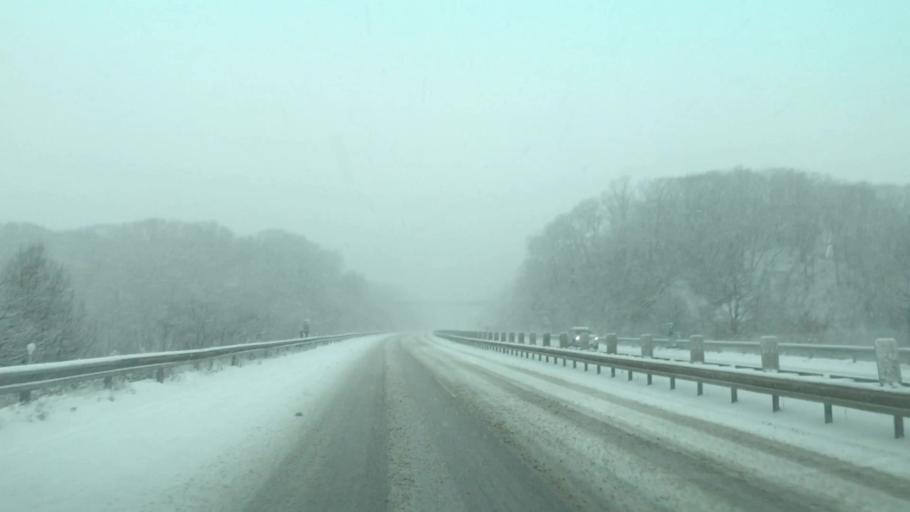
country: JP
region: Hokkaido
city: Muroran
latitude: 42.4386
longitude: 141.1365
